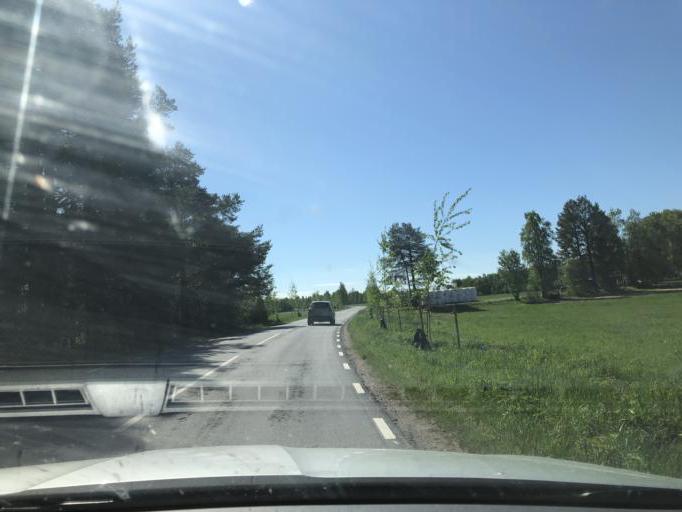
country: SE
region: Norrbotten
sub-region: Lulea Kommun
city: Gammelstad
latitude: 65.6541
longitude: 22.0160
